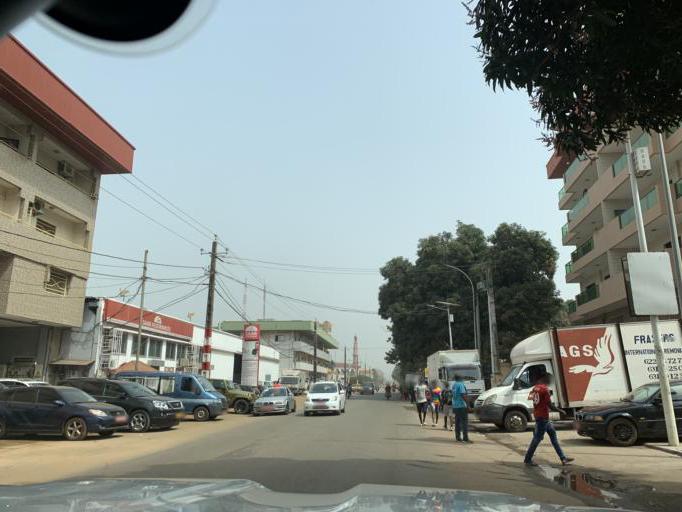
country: GN
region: Conakry
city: Camayenne
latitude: 9.5295
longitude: -13.6825
